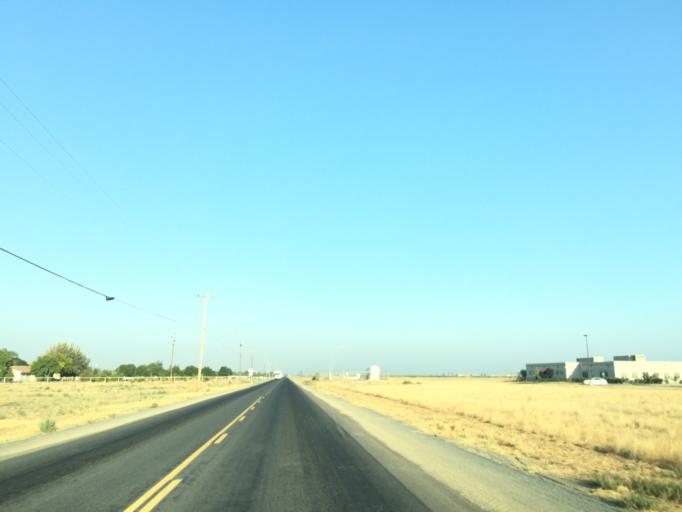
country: US
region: California
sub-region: Tulare County
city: Cutler
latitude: 36.4580
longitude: -119.3230
